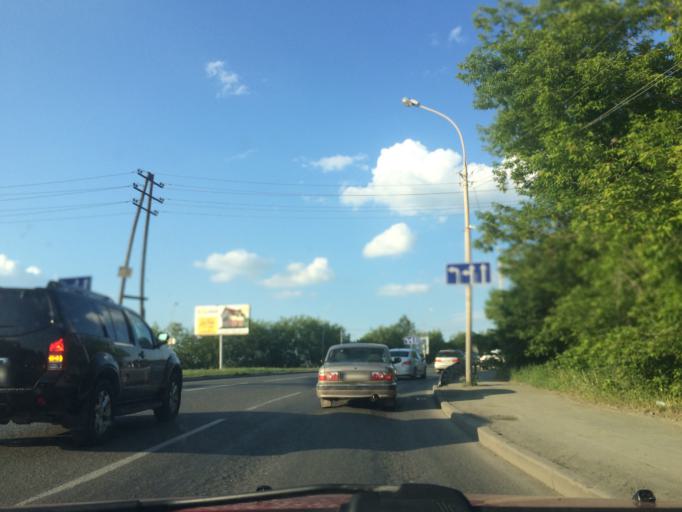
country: RU
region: Sverdlovsk
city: Yekaterinburg
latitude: 56.8299
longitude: 60.6645
